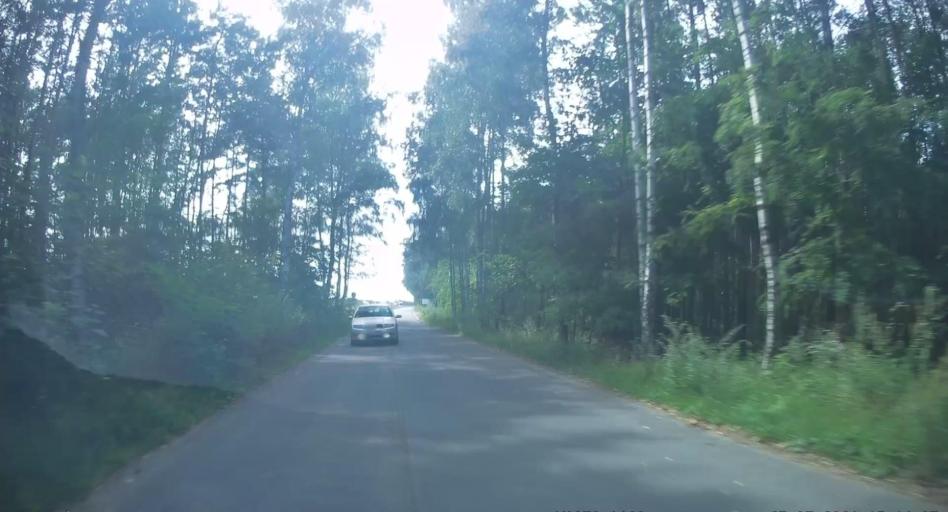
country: PL
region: Lodz Voivodeship
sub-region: Powiat rawski
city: Rawa Mazowiecka
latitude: 51.7013
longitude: 20.2326
